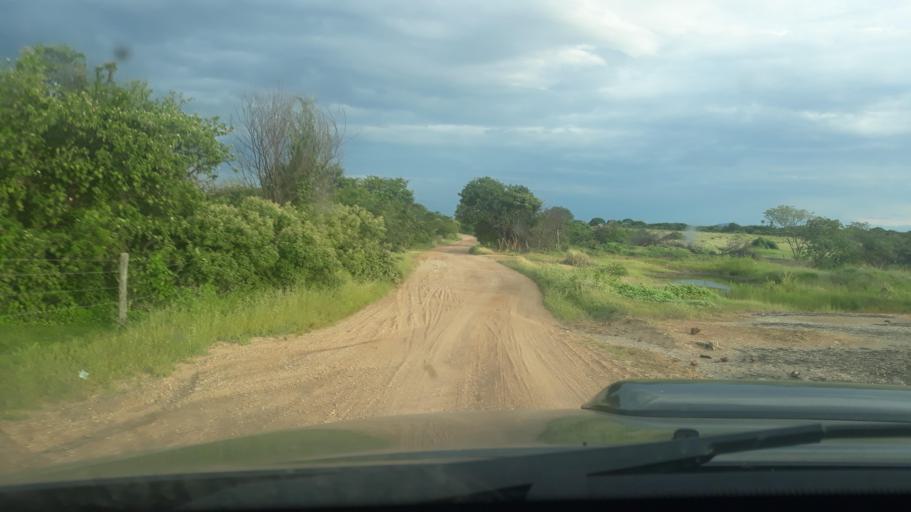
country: BR
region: Bahia
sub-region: Riacho De Santana
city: Riacho de Santana
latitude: -13.9073
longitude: -42.9675
